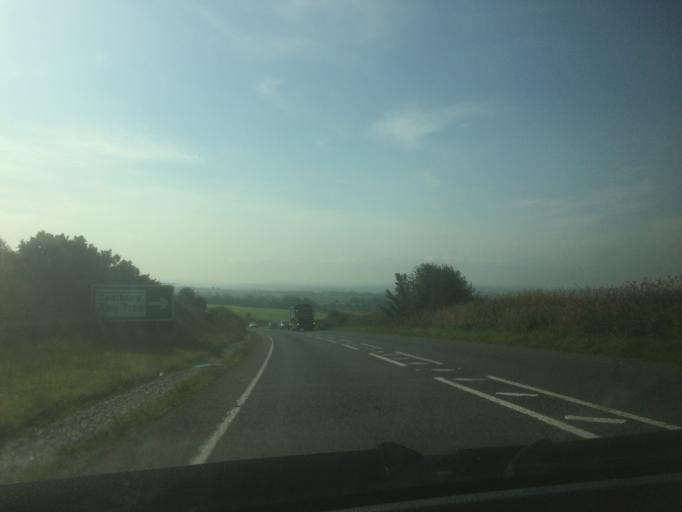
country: GB
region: England
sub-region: Cornwall
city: Pillaton
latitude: 50.4793
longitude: -4.2851
